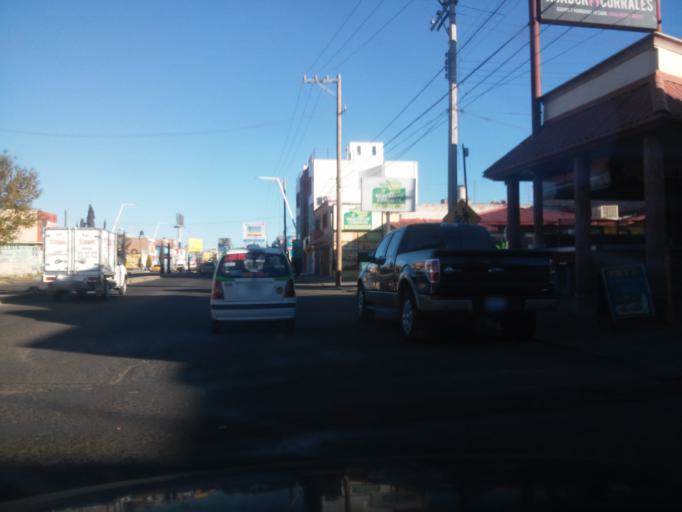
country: MX
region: Durango
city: Victoria de Durango
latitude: 24.0180
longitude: -104.6517
